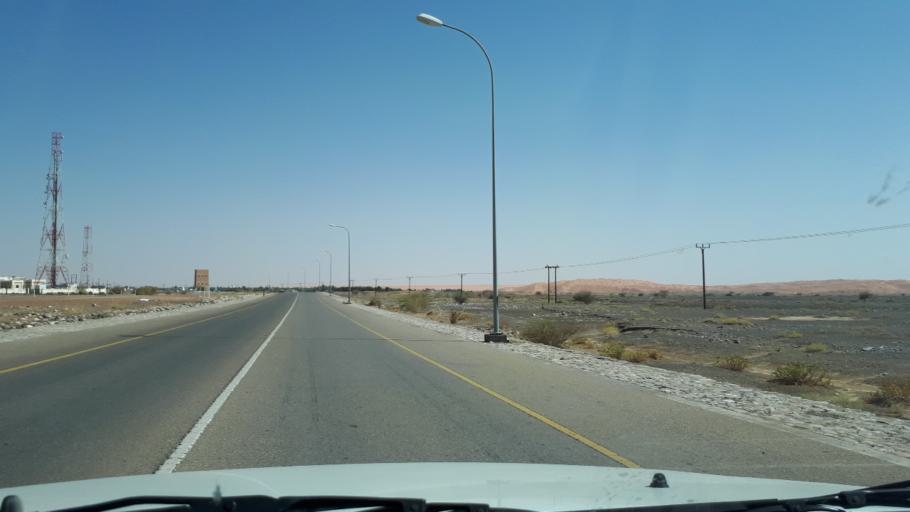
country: OM
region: Ash Sharqiyah
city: Al Qabil
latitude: 22.5164
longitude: 58.7375
